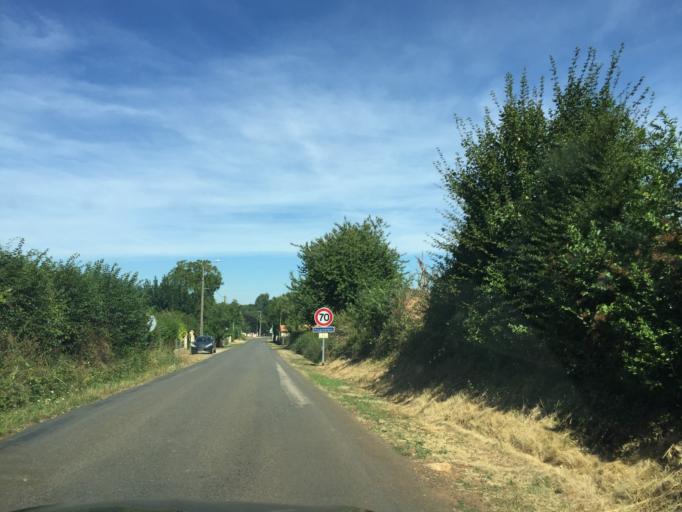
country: FR
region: Poitou-Charentes
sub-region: Departement de la Vienne
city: Iteuil
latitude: 46.4592
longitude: 0.3206
